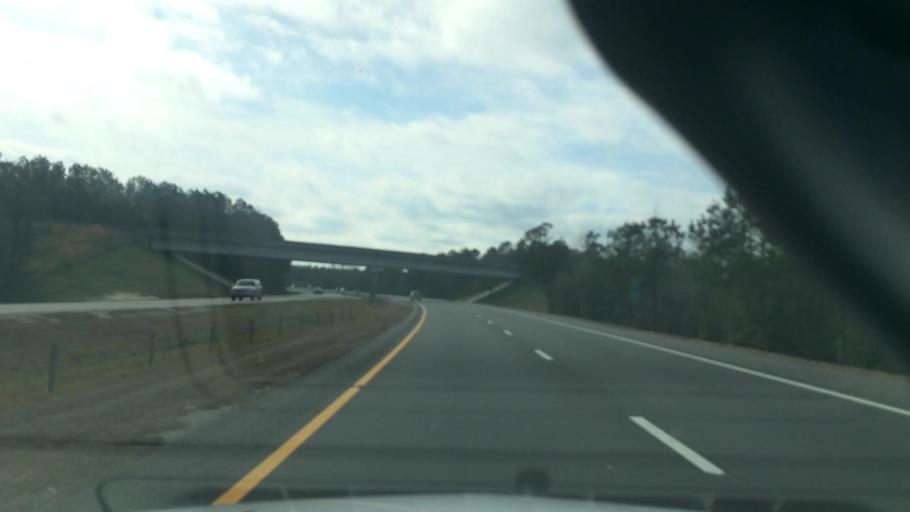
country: US
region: North Carolina
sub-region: New Hanover County
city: Wrightsboro
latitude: 34.3178
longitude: -77.9417
